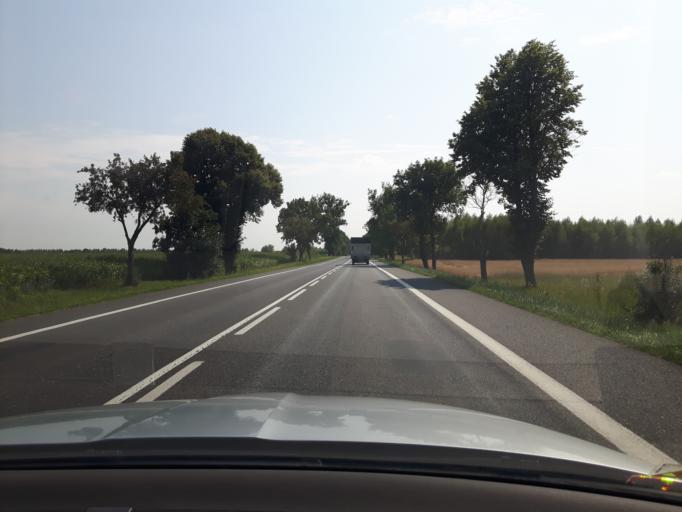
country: PL
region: Masovian Voivodeship
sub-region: Powiat mlawski
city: Wisniewo
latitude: 53.0171
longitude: 20.3334
